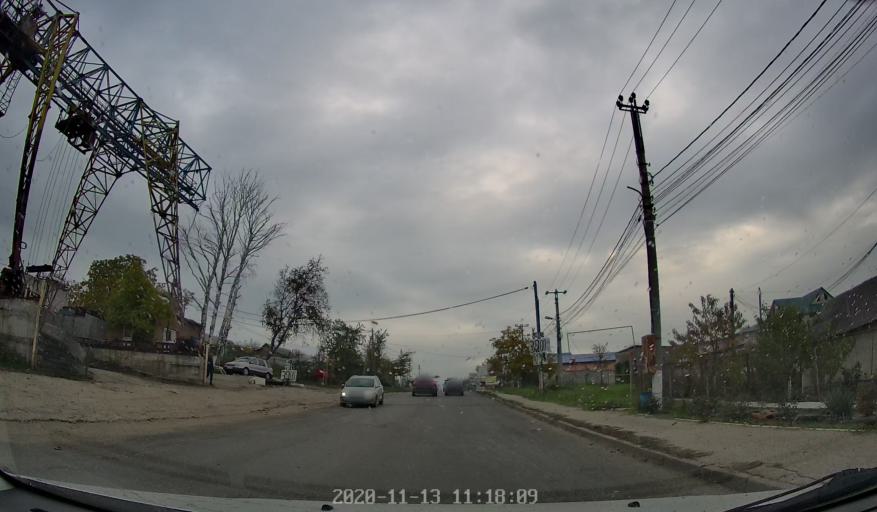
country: MD
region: Chisinau
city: Chisinau
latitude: 46.9918
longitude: 28.9113
